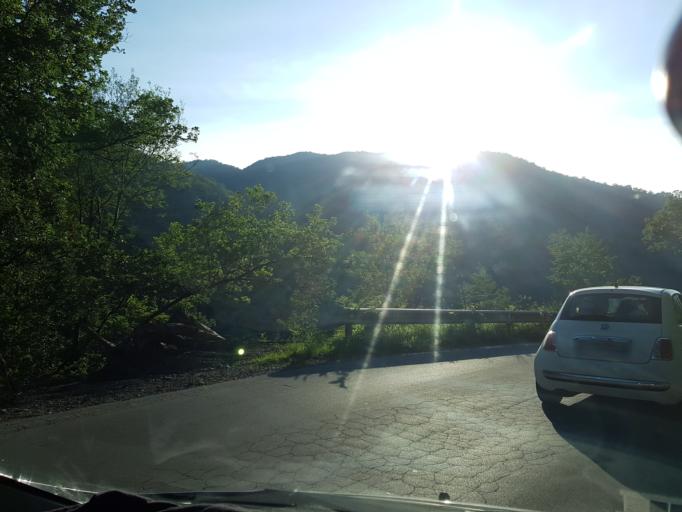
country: IT
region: Tuscany
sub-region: Provincia di Lucca
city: Minucciano
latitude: 44.1820
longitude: 10.1961
